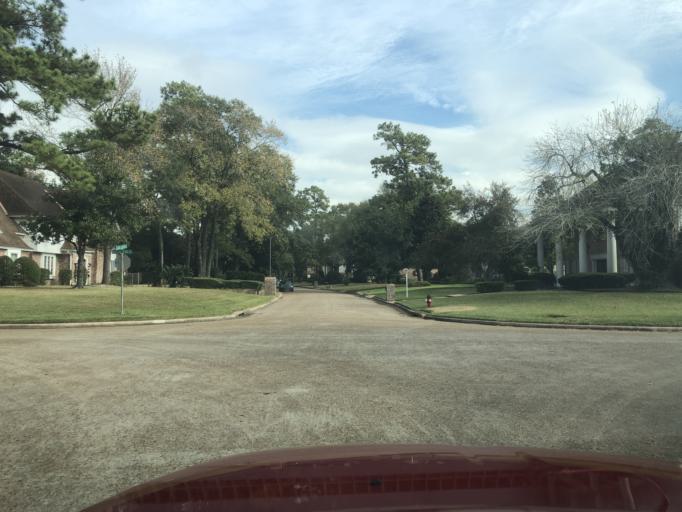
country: US
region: Texas
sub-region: Harris County
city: Spring
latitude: 30.0150
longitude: -95.4632
